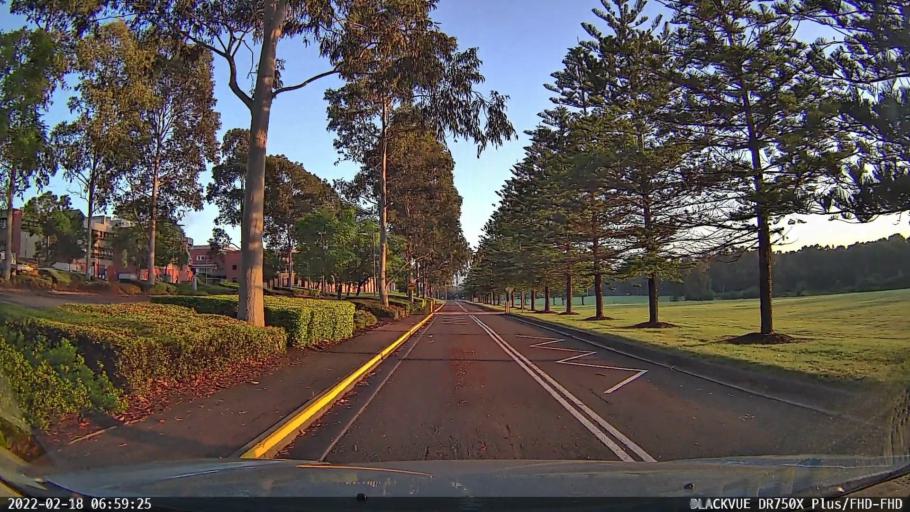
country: AU
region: New South Wales
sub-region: Penrith Municipality
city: Kingswood Park
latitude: -33.7683
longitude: 150.7301
